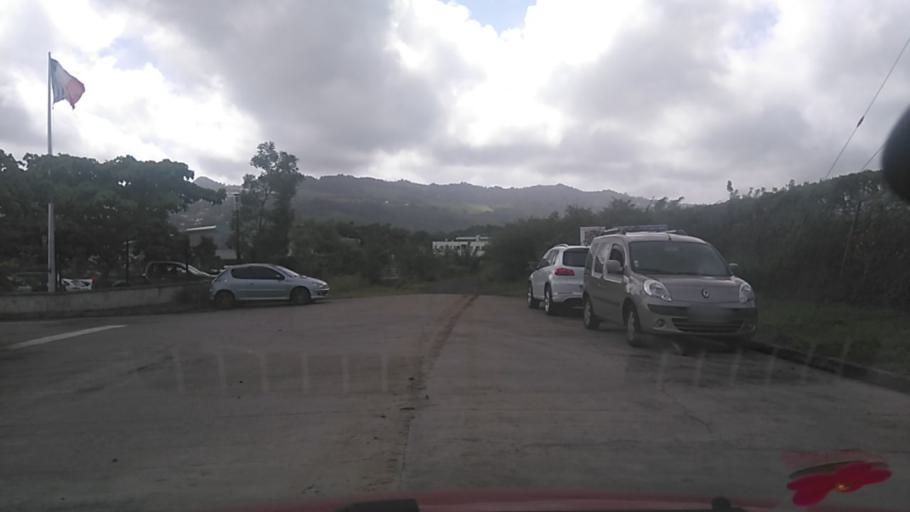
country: MQ
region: Martinique
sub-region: Martinique
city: Le Lamentin
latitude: 14.6275
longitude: -60.9887
